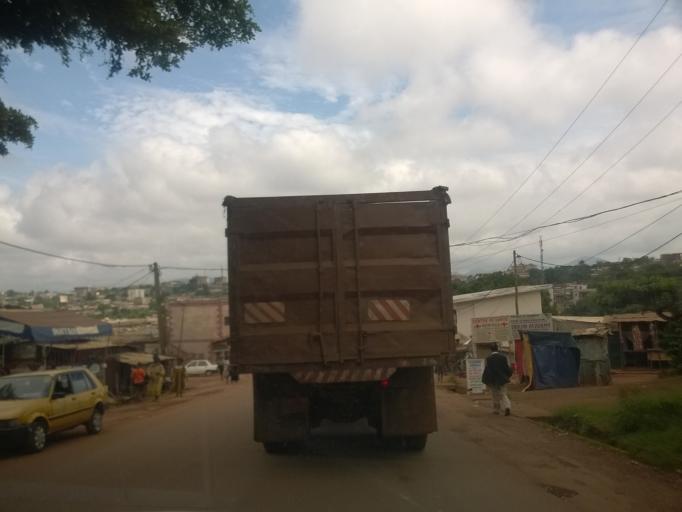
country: CM
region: Centre
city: Yaounde
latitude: 3.8694
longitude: 11.5455
